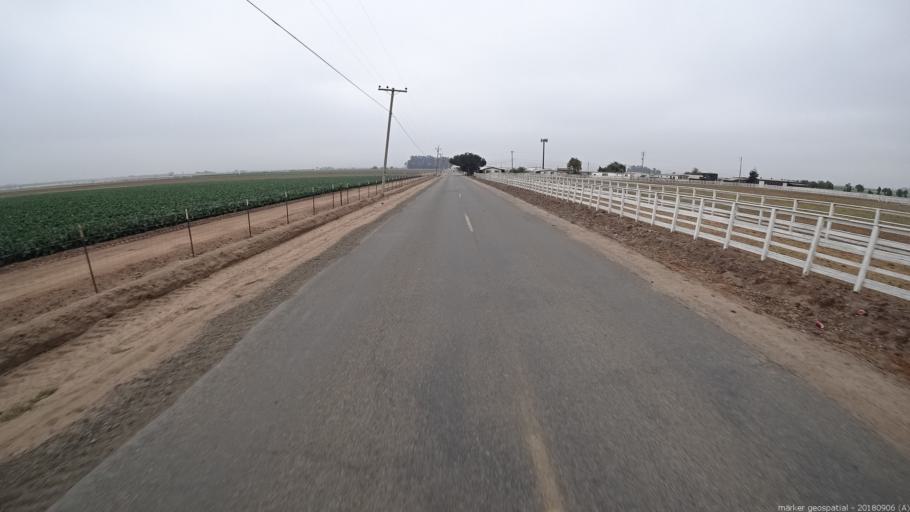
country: US
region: California
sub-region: Monterey County
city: Chualar
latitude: 36.6609
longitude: -121.5540
